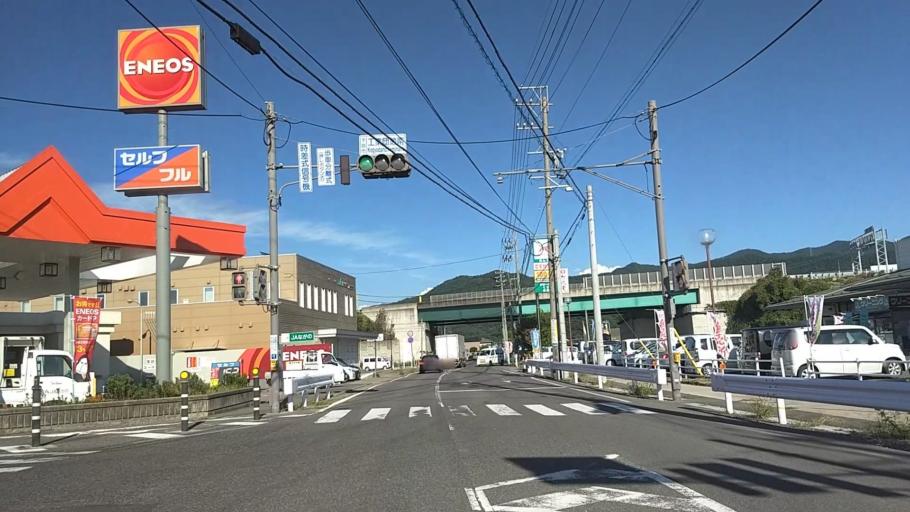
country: JP
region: Nagano
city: Nagano-shi
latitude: 36.5462
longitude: 138.1376
